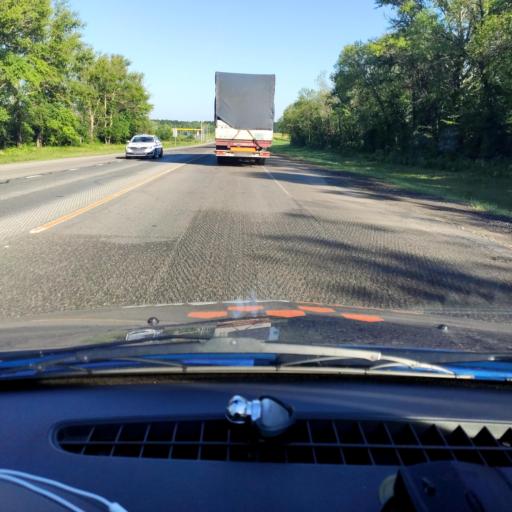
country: RU
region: Orjol
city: Zmiyevka
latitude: 52.7084
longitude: 36.3585
